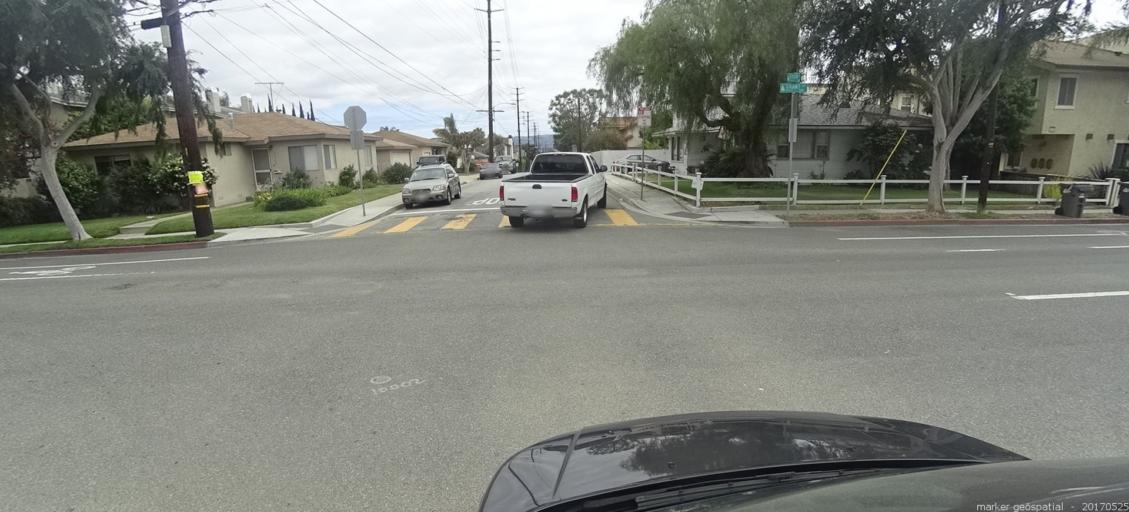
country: US
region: California
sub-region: Los Angeles County
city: Redondo Beach
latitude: 33.8691
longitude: -118.3749
